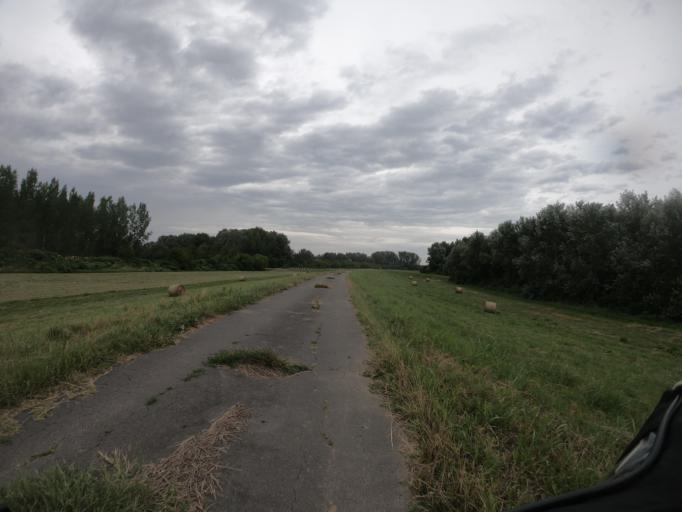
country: HU
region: Hajdu-Bihar
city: Tiszacsege
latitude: 47.7175
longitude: 20.9410
